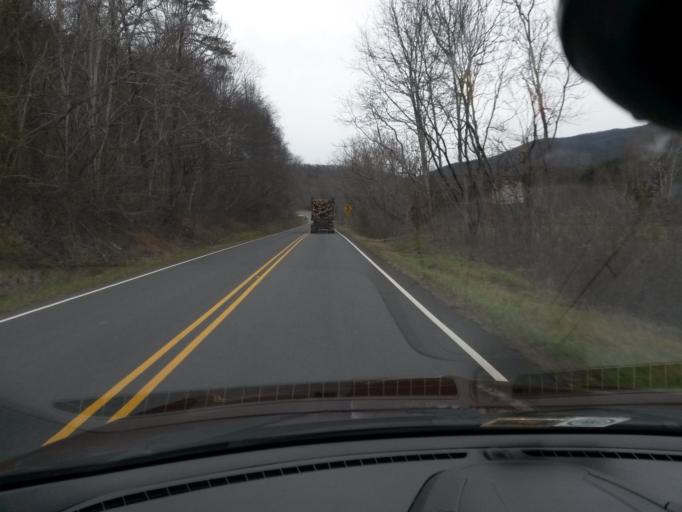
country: US
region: Virginia
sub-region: City of Buena Vista
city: Buena Vista
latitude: 37.6881
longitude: -79.2394
